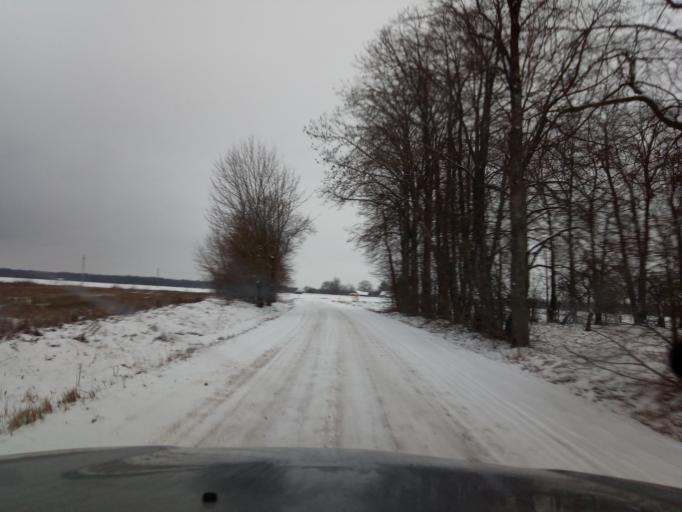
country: LT
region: Vilnius County
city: Ukmerge
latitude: 55.4861
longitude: 24.5890
